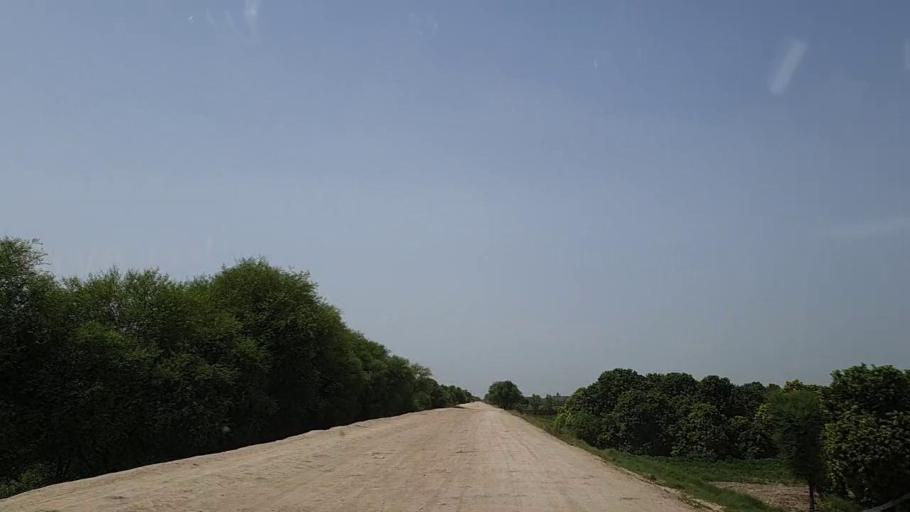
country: PK
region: Sindh
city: Tharu Shah
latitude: 27.0273
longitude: 68.1157
